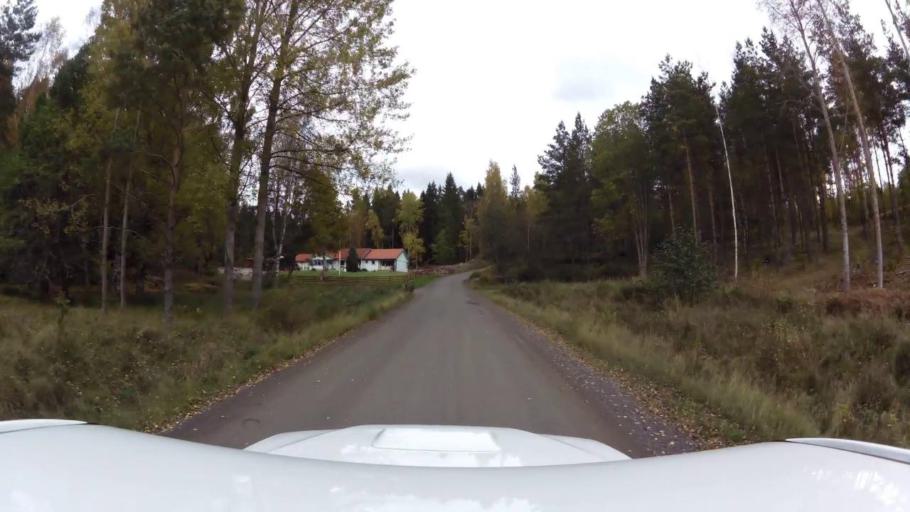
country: SE
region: OEstergoetland
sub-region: Linkopings Kommun
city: Berg
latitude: 58.5427
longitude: 15.5921
